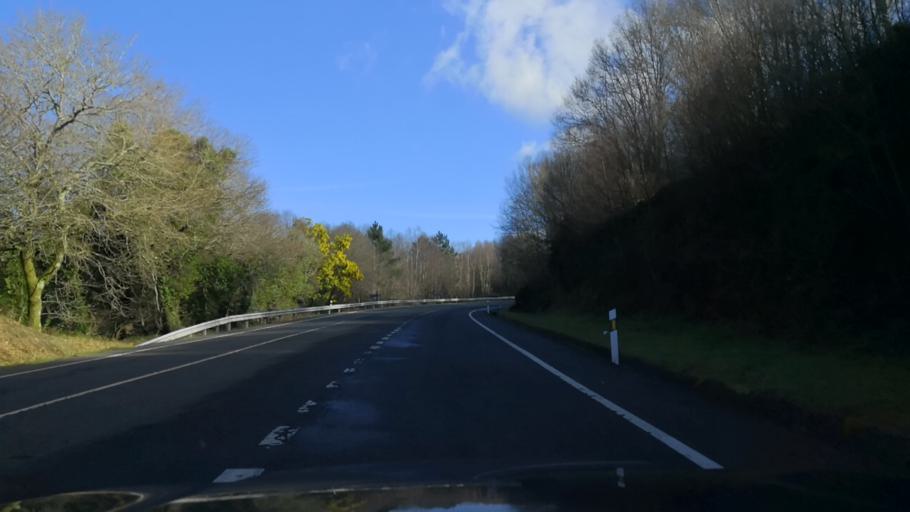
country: ES
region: Galicia
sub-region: Provincia da Coruna
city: Ribeira
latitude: 42.7148
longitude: -8.3614
